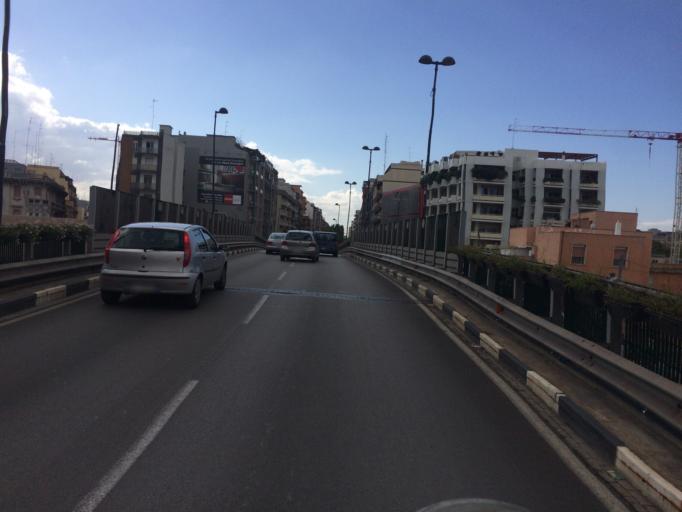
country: IT
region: Apulia
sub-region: Provincia di Bari
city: Bari
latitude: 41.1182
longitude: 16.8728
